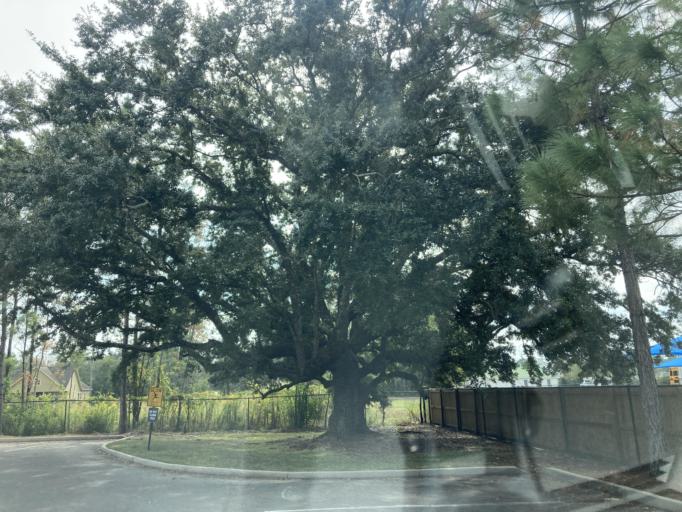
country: US
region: Mississippi
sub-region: Jackson County
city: Gulf Hills
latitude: 30.4483
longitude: -88.8386
